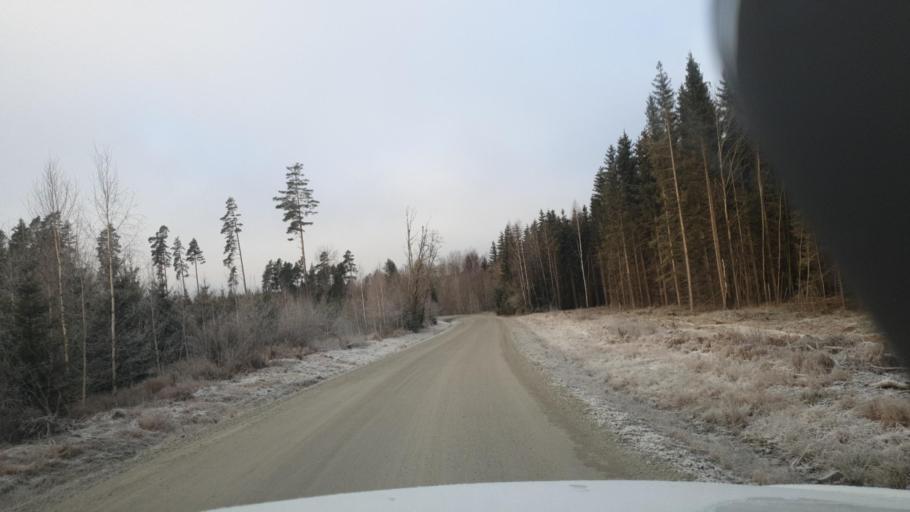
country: SE
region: Vaermland
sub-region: Karlstads Kommun
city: Edsvalla
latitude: 59.4414
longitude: 13.1846
